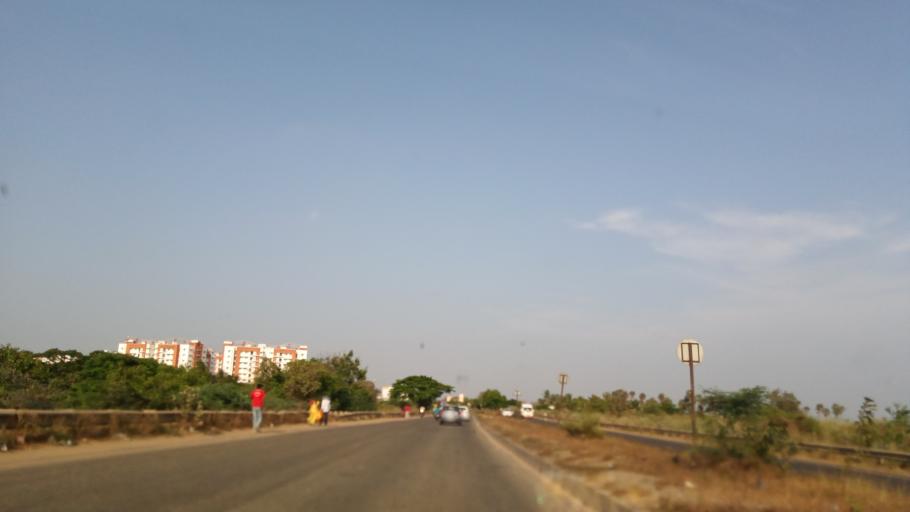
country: IN
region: Tamil Nadu
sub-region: Kancheepuram
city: Nandambakkam
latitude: 13.0225
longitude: 80.0177
